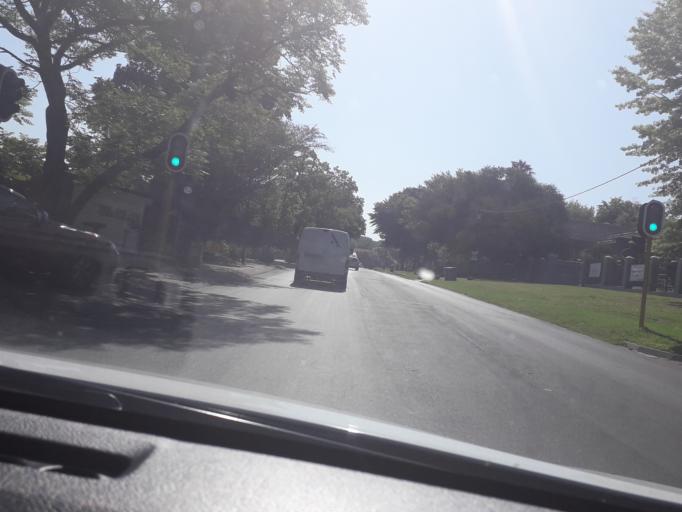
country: ZA
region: Gauteng
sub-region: City of Johannesburg Metropolitan Municipality
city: Johannesburg
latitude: -26.0821
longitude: 28.0212
